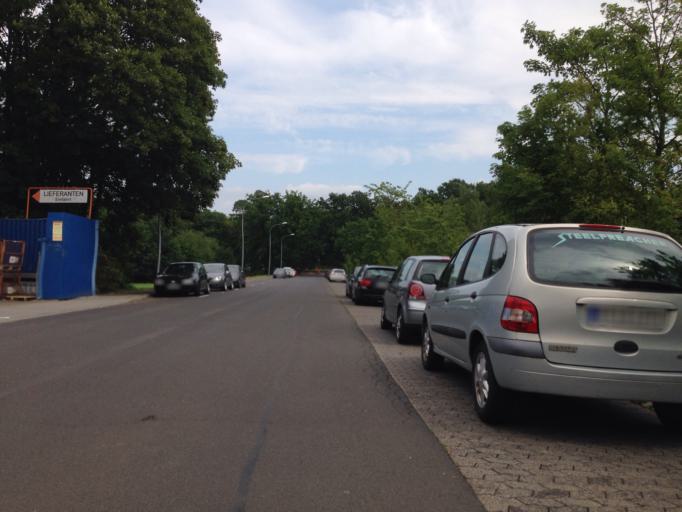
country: DE
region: Hesse
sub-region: Regierungsbezirk Giessen
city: Giessen
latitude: 50.5720
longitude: 8.6970
